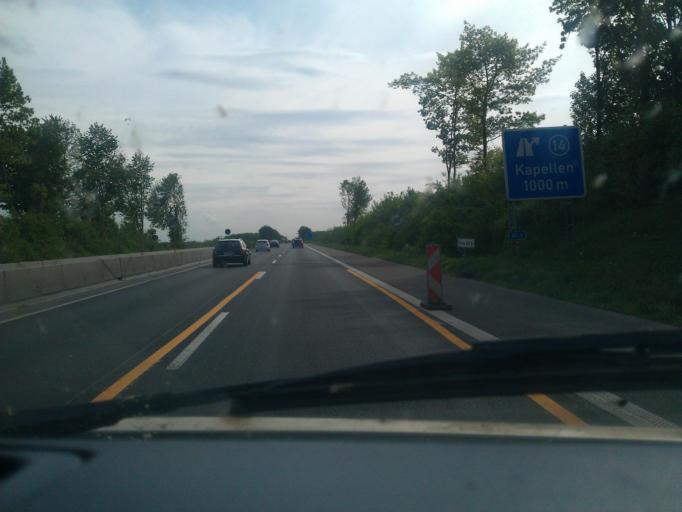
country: DE
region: North Rhine-Westphalia
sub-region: Regierungsbezirk Dusseldorf
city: Neubrueck
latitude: 51.1506
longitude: 6.6302
